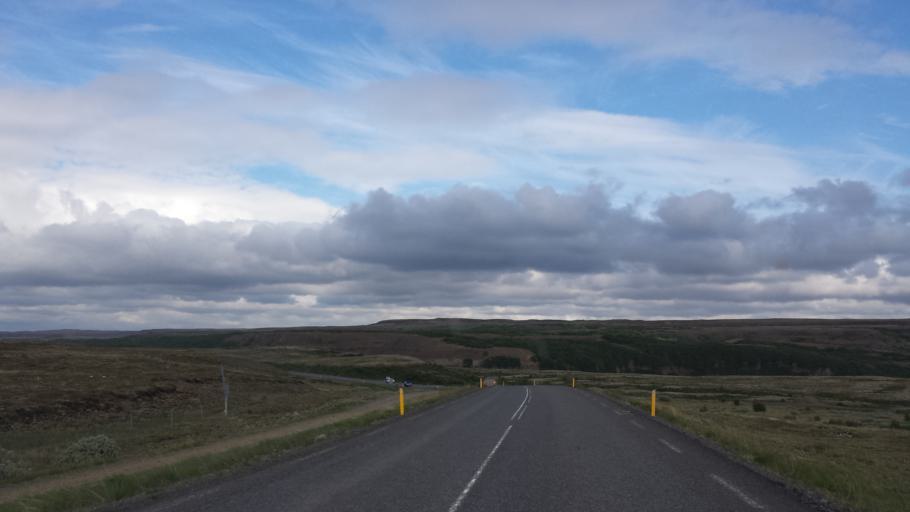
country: IS
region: South
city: Vestmannaeyjar
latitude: 64.3055
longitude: -20.1732
